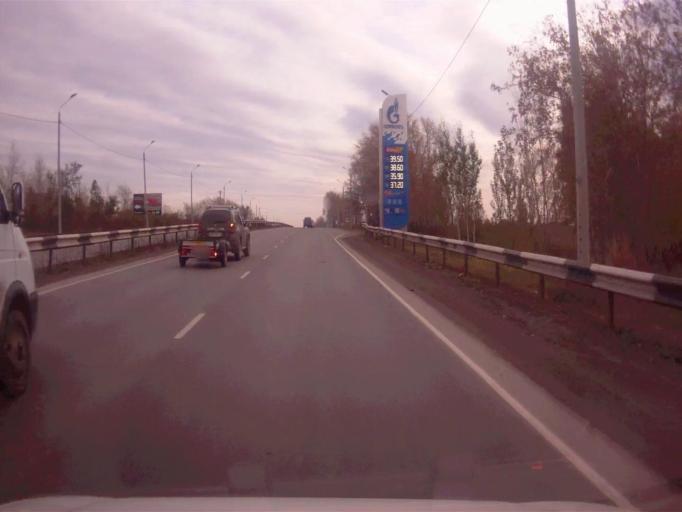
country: RU
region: Chelyabinsk
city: Novosineglazovskiy
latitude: 55.0571
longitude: 61.4056
